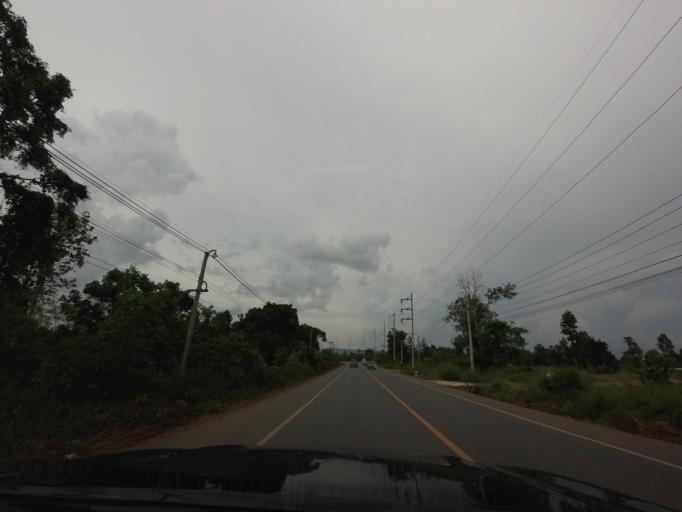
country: TH
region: Changwat Nong Bua Lamphu
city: Nong Bua Lamphu
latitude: 17.1021
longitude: 102.3936
